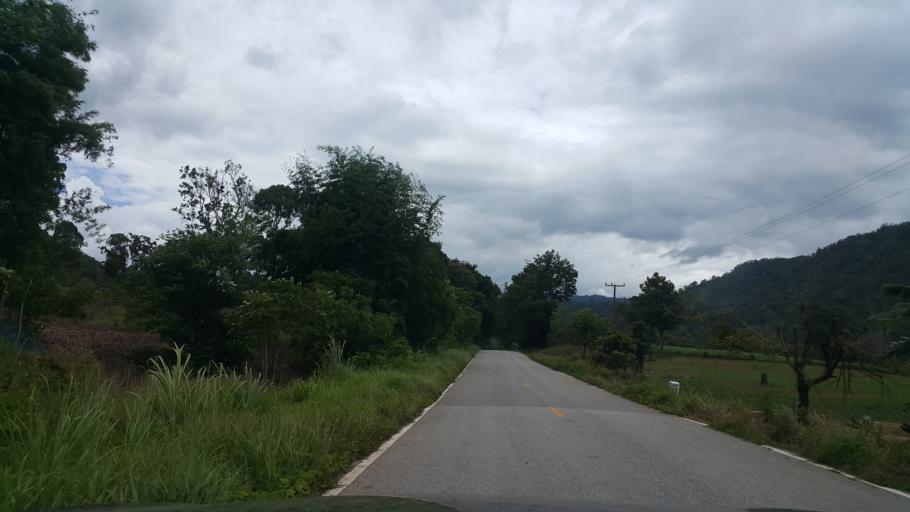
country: TH
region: Phitsanulok
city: Chat Trakan
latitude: 17.3734
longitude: 100.7439
